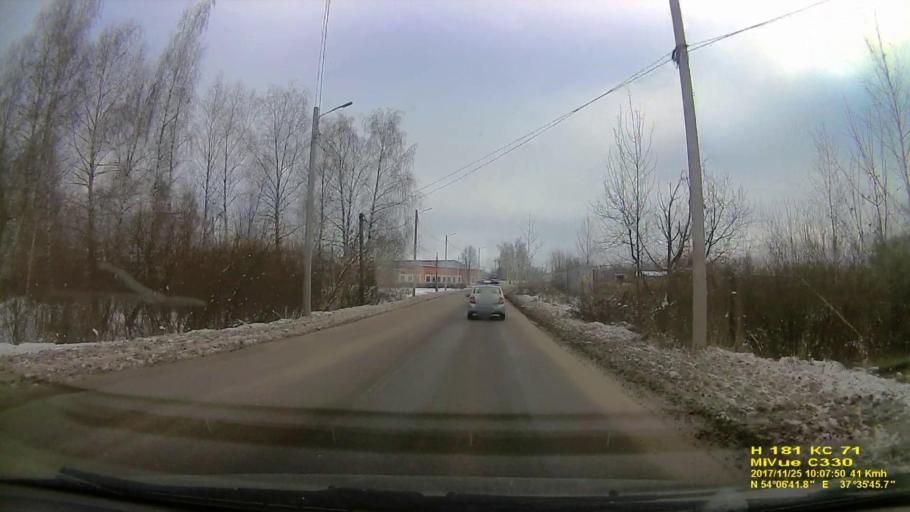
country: RU
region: Tula
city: Skuratovskiy
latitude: 54.1115
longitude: 37.5964
